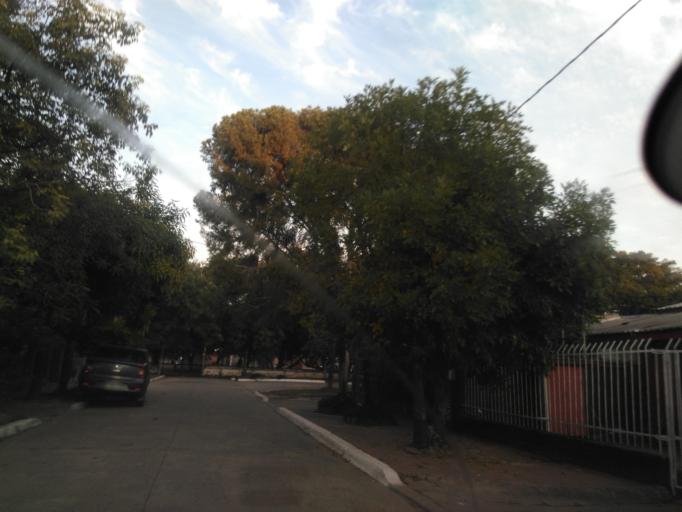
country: AR
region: Chaco
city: Resistencia
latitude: -27.4533
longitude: -59.0166
